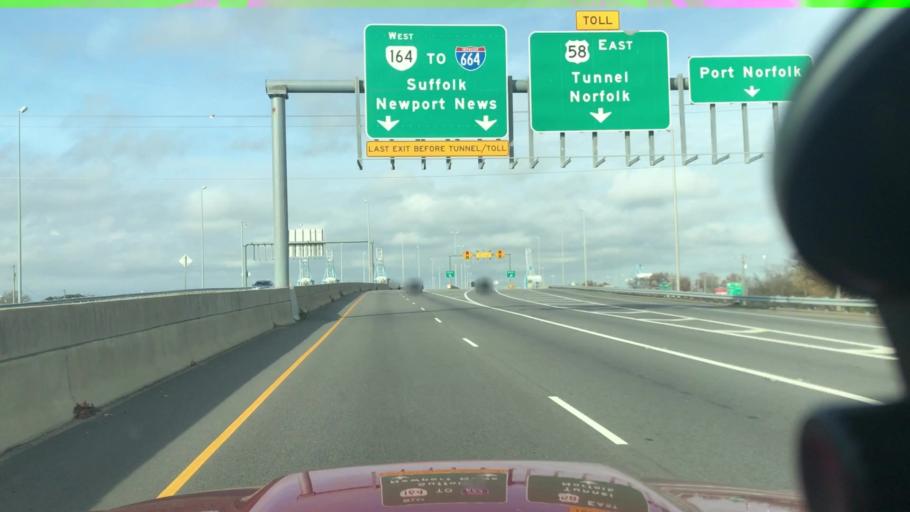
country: US
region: Virginia
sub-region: City of Portsmouth
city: Portsmouth
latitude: 36.8446
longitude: -76.3294
